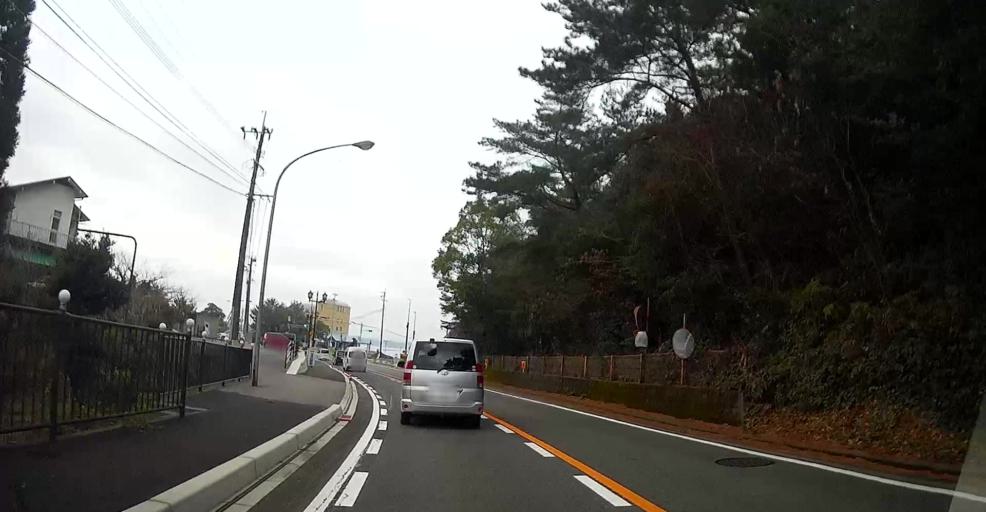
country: JP
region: Kumamoto
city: Yatsushiro
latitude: 32.5253
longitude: 130.4247
